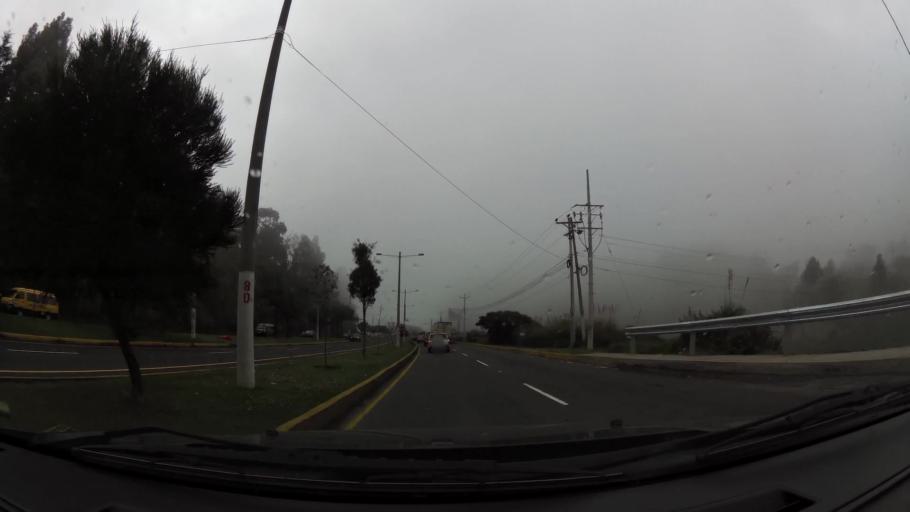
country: EC
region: Pichincha
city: Quito
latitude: -0.2468
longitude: -78.4846
